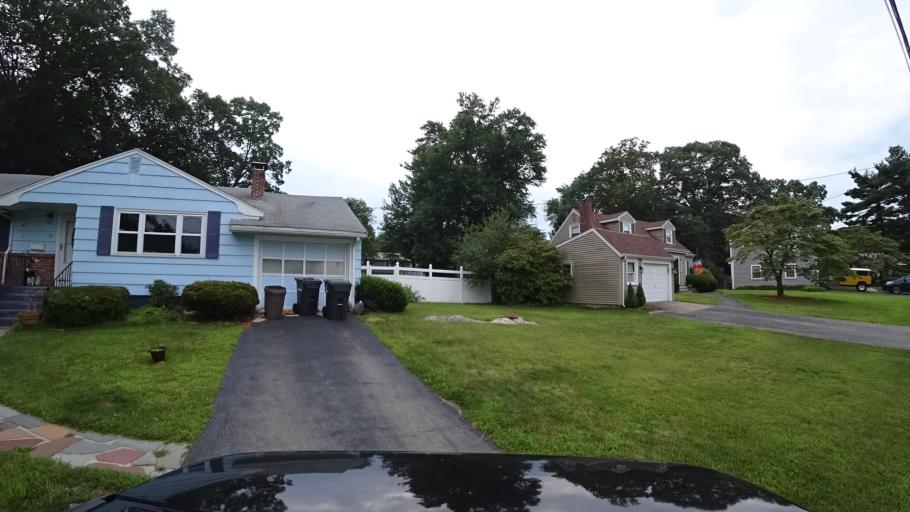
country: US
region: Massachusetts
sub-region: Norfolk County
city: Dedham
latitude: 42.2256
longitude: -71.1608
